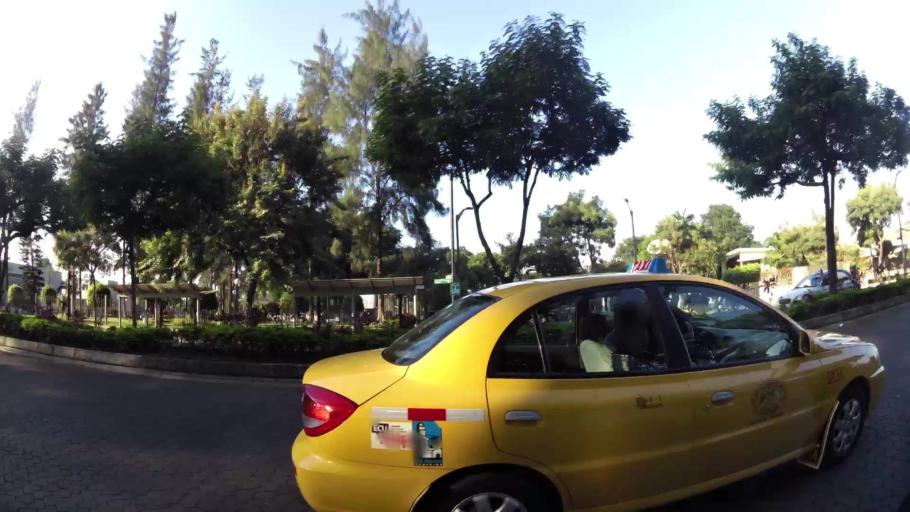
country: EC
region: Guayas
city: Guayaquil
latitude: -2.1763
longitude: -79.9045
